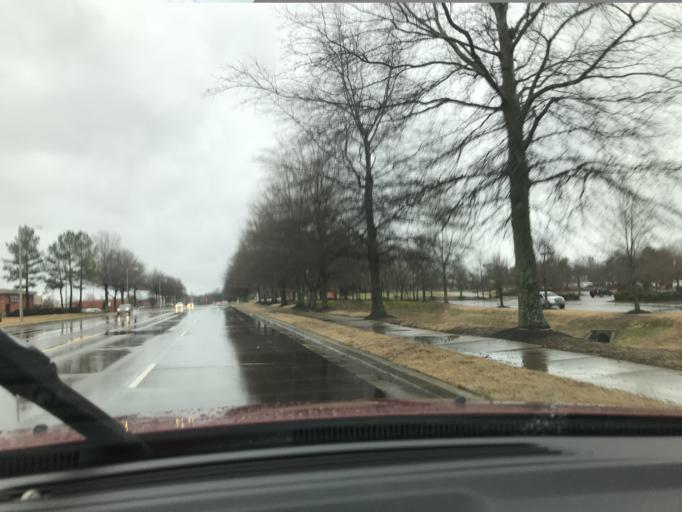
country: US
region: Tennessee
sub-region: Shelby County
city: Collierville
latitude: 35.0506
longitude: -89.6944
